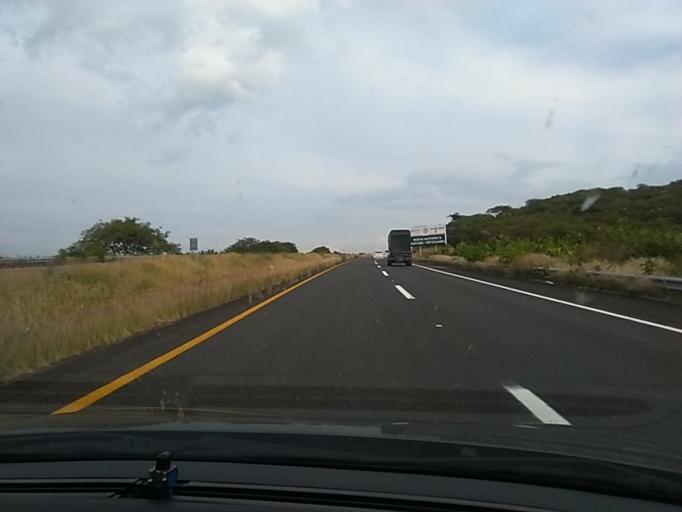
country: MX
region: Michoacan
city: Copandaro de Galeana
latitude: 19.8904
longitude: -101.2363
